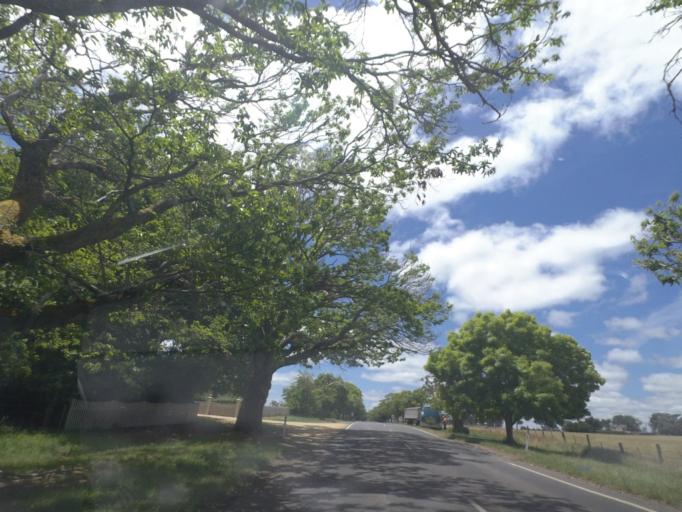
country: AU
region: Victoria
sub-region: Mount Alexander
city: Castlemaine
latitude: -37.3381
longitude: 144.1603
